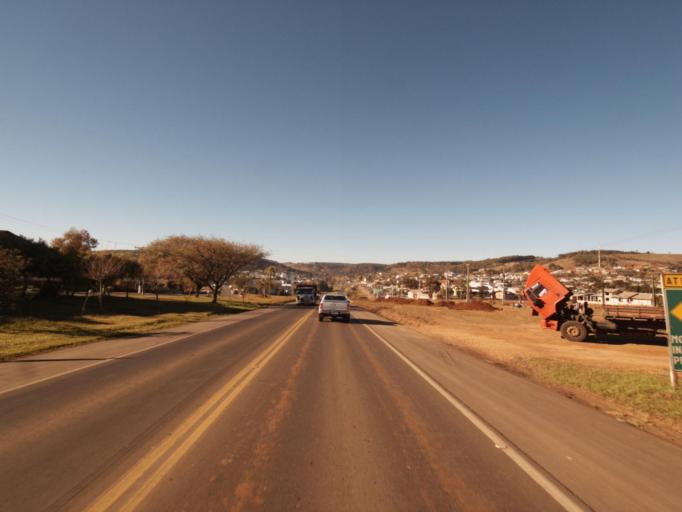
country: BR
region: Santa Catarina
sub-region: Concordia
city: Concordia
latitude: -26.8670
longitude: -52.0224
